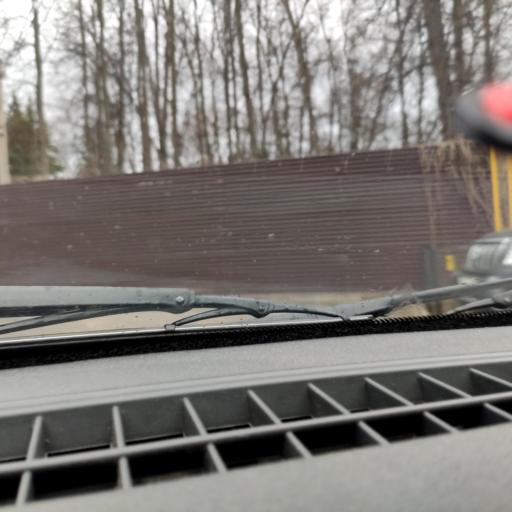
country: RU
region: Bashkortostan
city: Ufa
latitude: 54.6772
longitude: 56.0103
